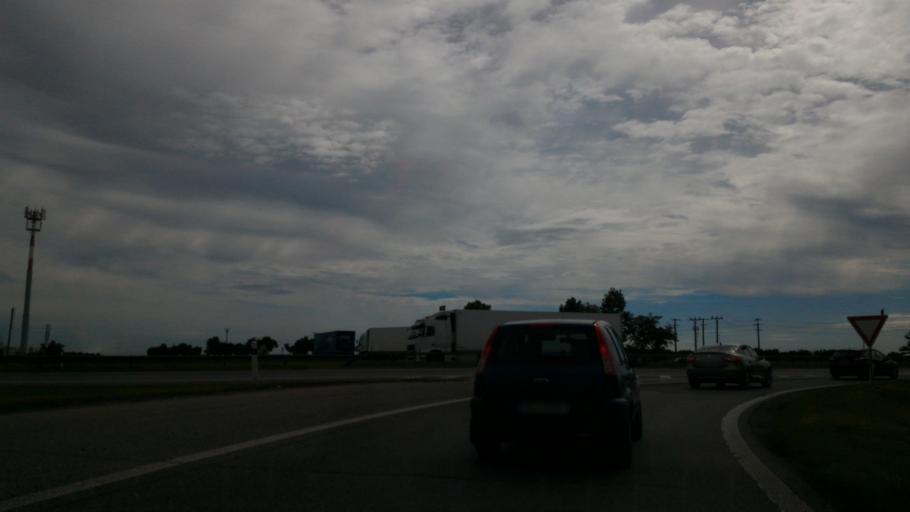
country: CZ
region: Central Bohemia
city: Zdiby
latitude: 50.1759
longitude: 14.4523
